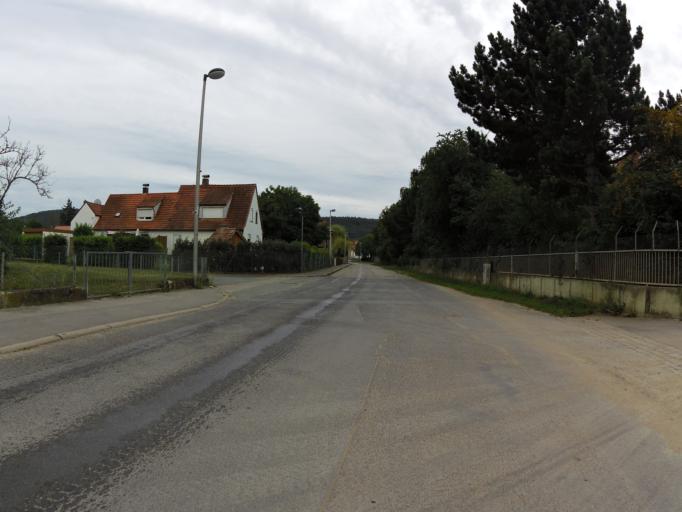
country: DE
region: Bavaria
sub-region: Regierungsbezirk Unterfranken
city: Sand
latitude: 49.9928
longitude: 10.5875
